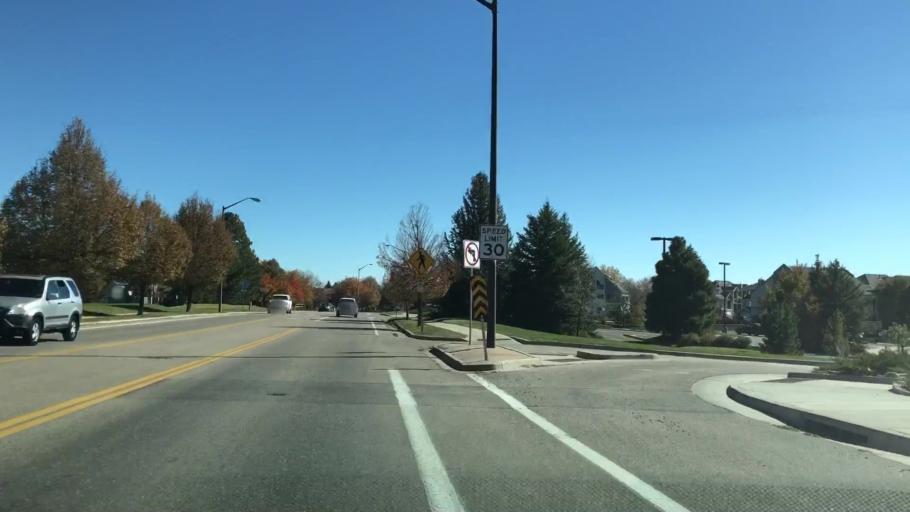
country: US
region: Colorado
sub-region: Larimer County
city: Fort Collins
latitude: 40.5319
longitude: -105.0735
